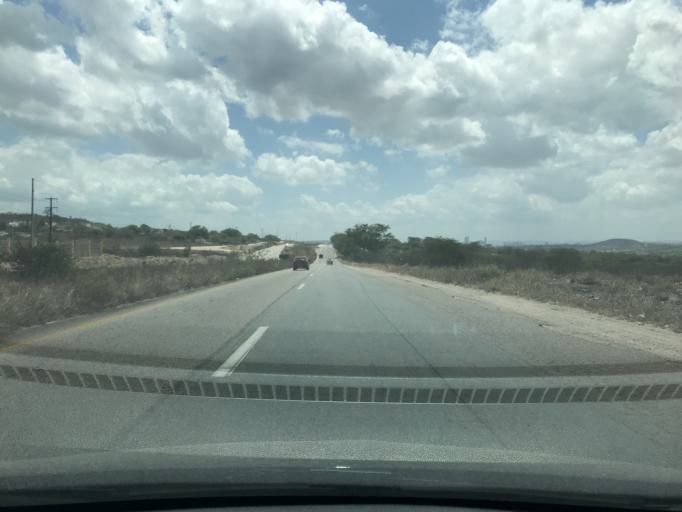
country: BR
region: Pernambuco
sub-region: Caruaru
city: Caruaru
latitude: -8.2946
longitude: -35.8859
